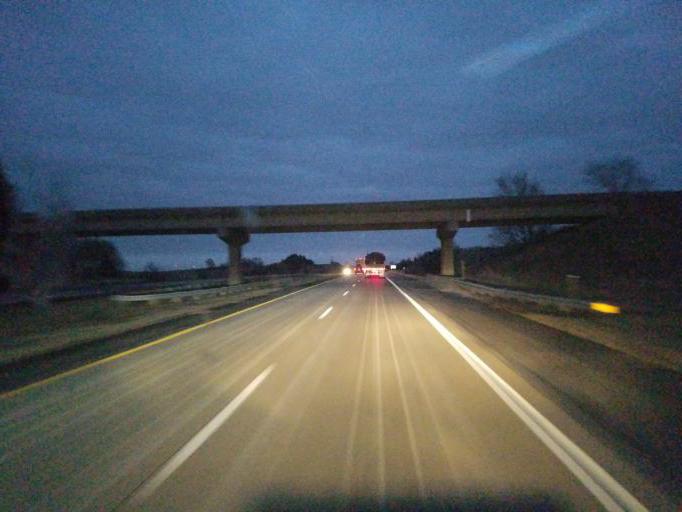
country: US
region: Iowa
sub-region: Cass County
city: Atlantic
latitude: 41.4964
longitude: -94.7779
